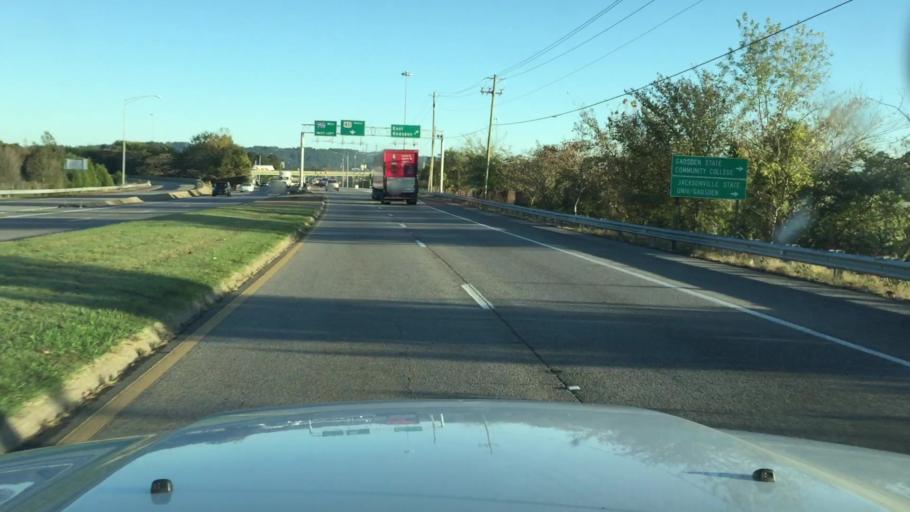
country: US
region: Alabama
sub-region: Etowah County
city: Gadsden
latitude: 33.9883
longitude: -86.0044
